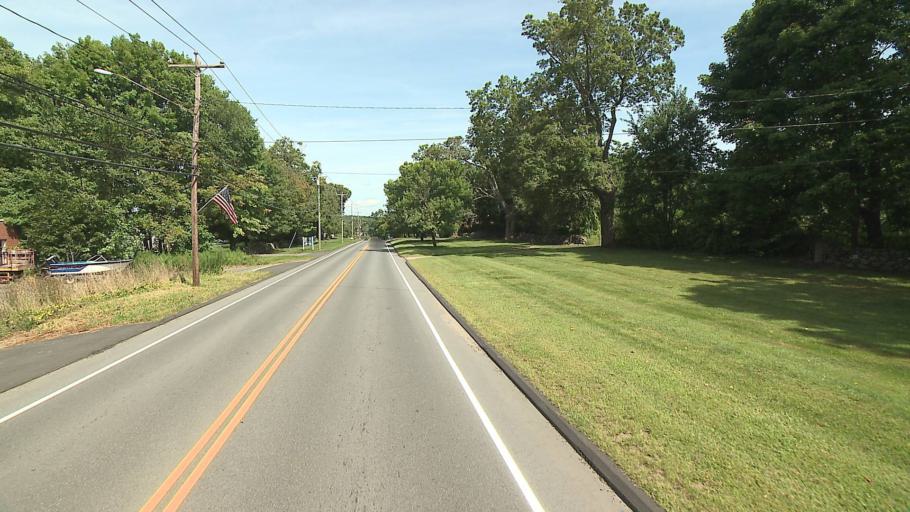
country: US
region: Connecticut
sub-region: Litchfield County
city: Bethlehem Village
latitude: 41.6314
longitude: -73.2087
